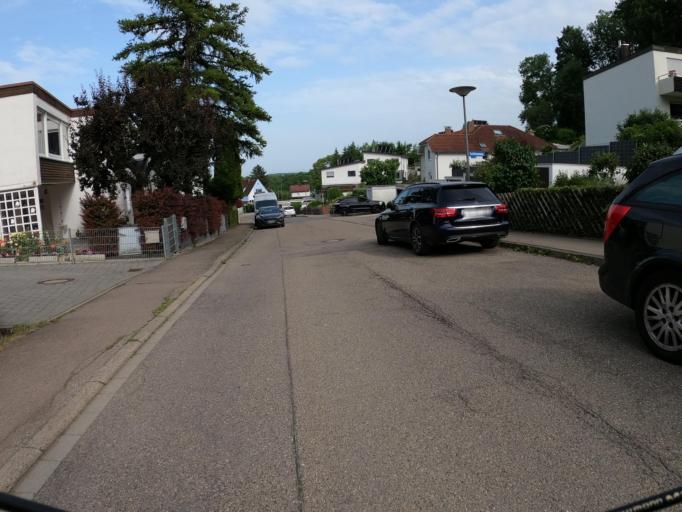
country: DE
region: Bavaria
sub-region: Swabia
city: Neu-Ulm
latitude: 48.4344
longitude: 10.0422
